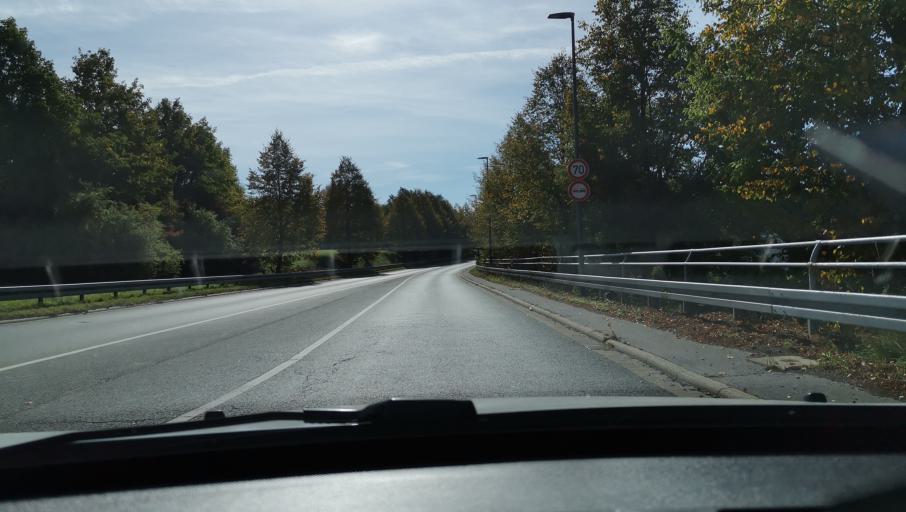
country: DE
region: North Rhine-Westphalia
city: Halver
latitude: 51.1956
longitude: 7.4938
